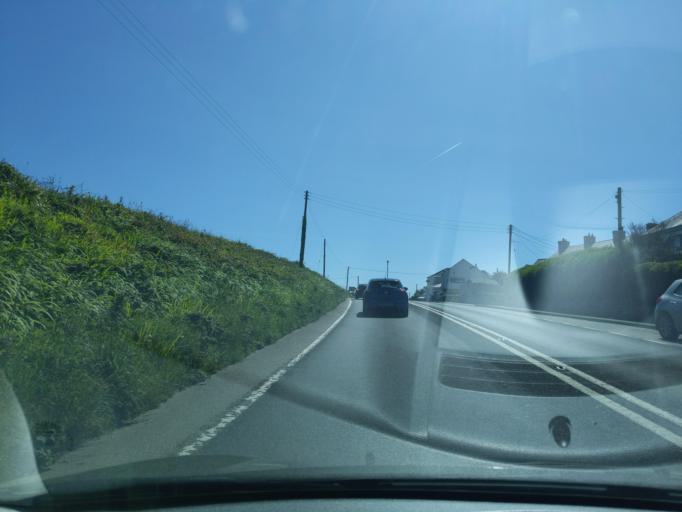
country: GB
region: England
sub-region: Cornwall
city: Wendron
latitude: 50.1624
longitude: -5.1825
